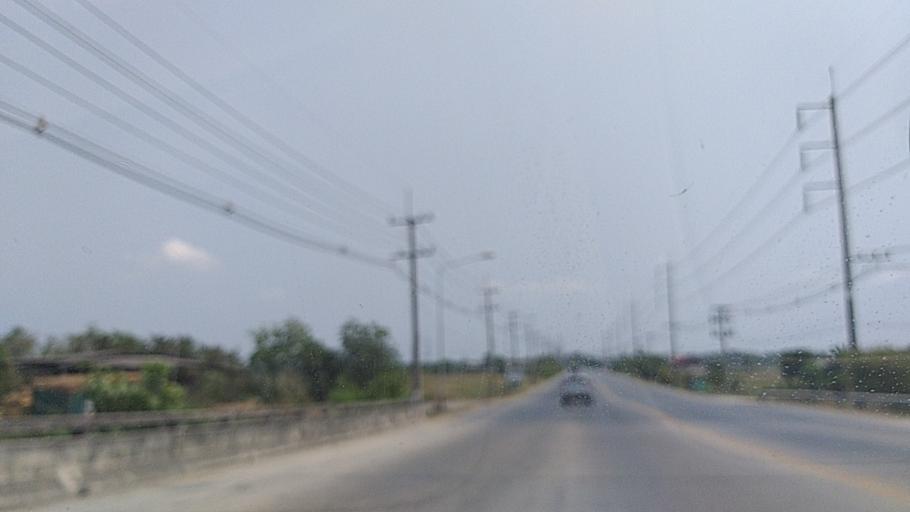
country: TH
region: Bangkok
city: Nong Chok
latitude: 13.9643
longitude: 100.9150
